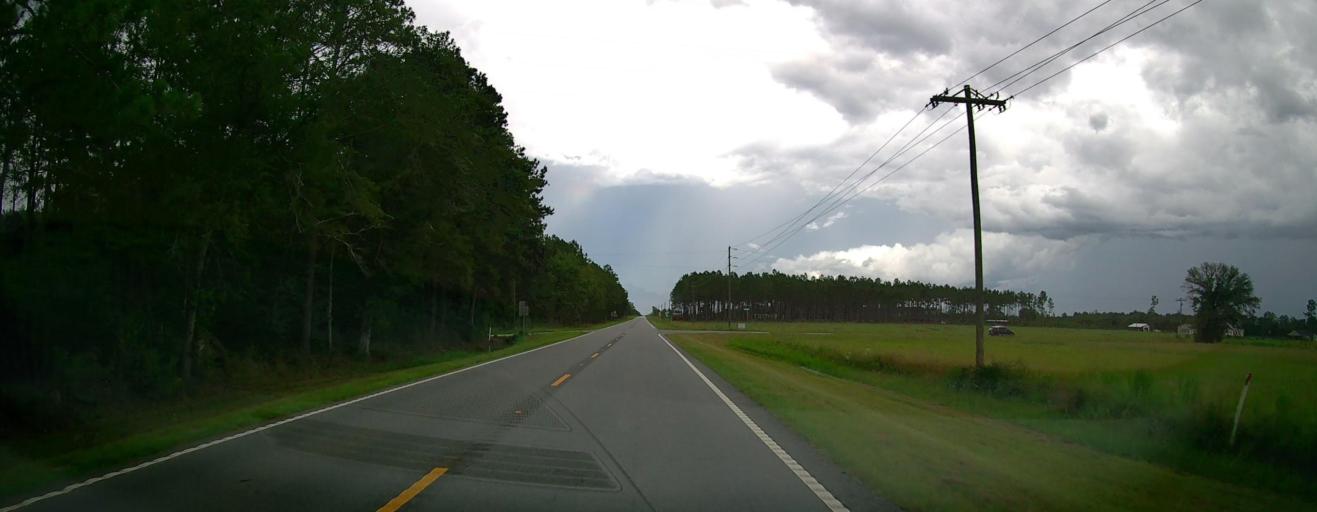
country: US
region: Georgia
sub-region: Pierce County
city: Blackshear
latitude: 31.3760
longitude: -82.1197
